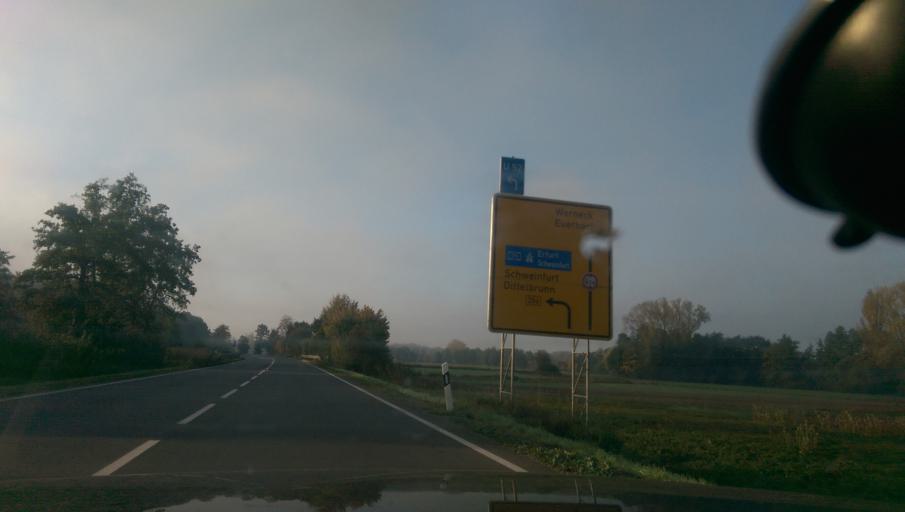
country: DE
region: Bavaria
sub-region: Regierungsbezirk Unterfranken
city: Poppenhausen
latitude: 50.0961
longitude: 10.1479
